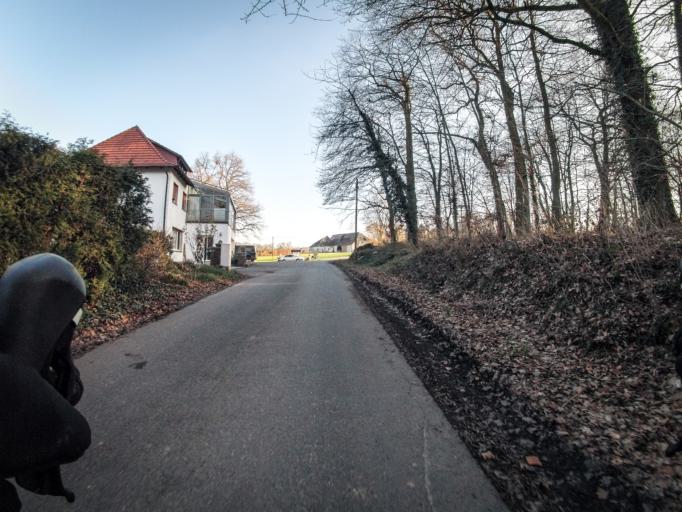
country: DE
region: North Rhine-Westphalia
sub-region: Regierungsbezirk Munster
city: Tecklenburg
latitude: 52.2578
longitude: 7.8338
